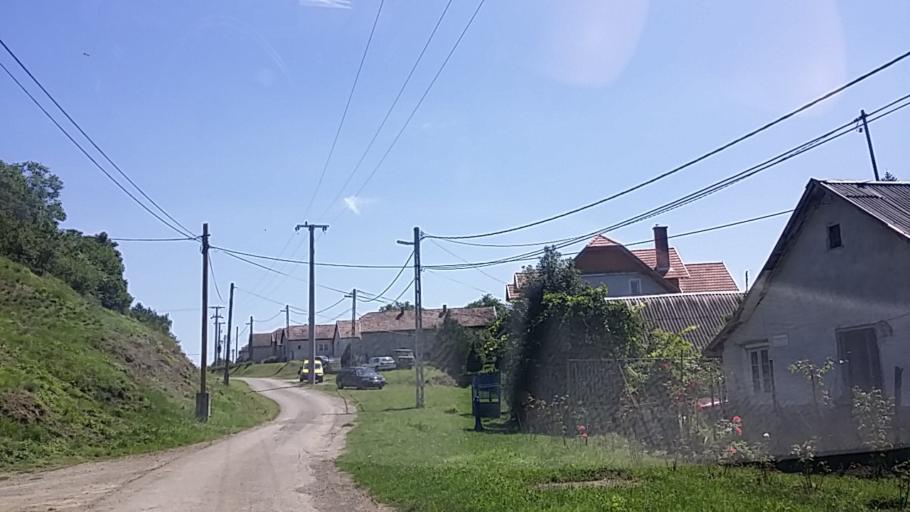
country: HU
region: Pest
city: Szob
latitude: 47.8659
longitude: 18.8679
